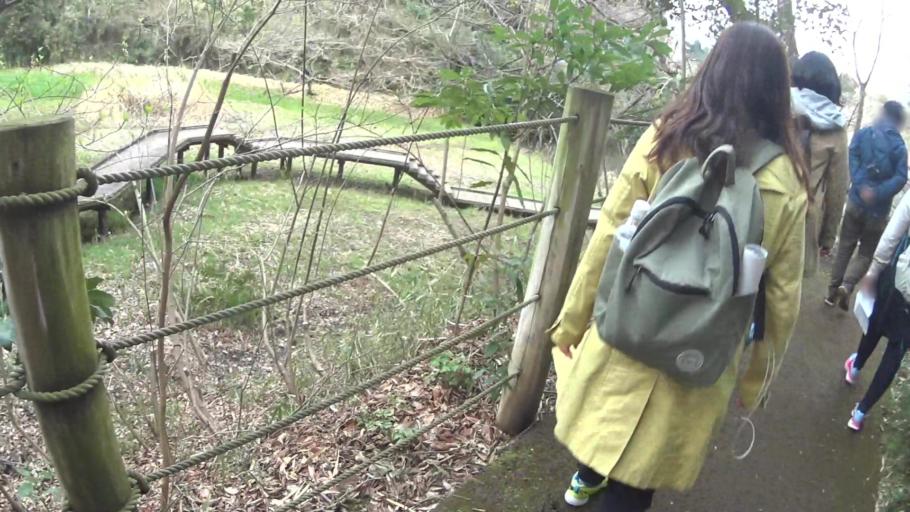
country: JP
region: Kanagawa
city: Kamakura
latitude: 35.3208
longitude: 139.5165
